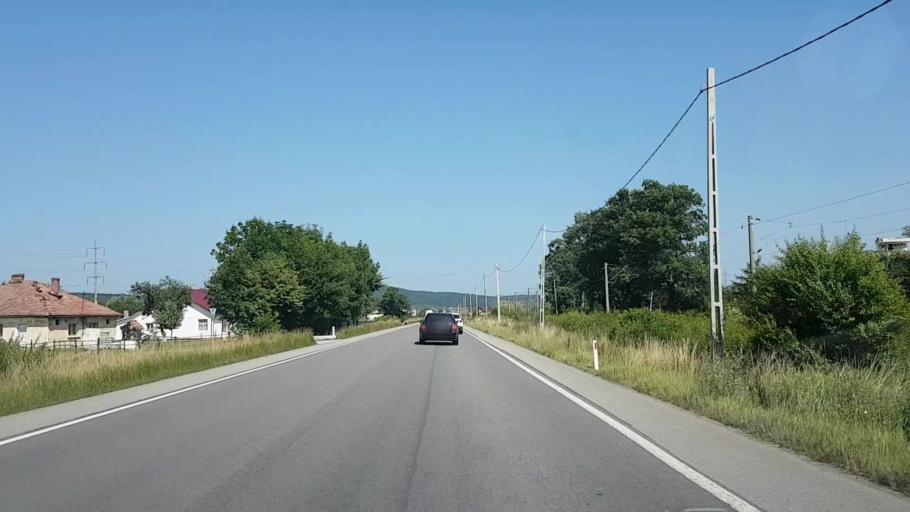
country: RO
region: Bistrita-Nasaud
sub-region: Comuna Sintereag
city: Cociu
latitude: 47.1814
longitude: 24.2575
